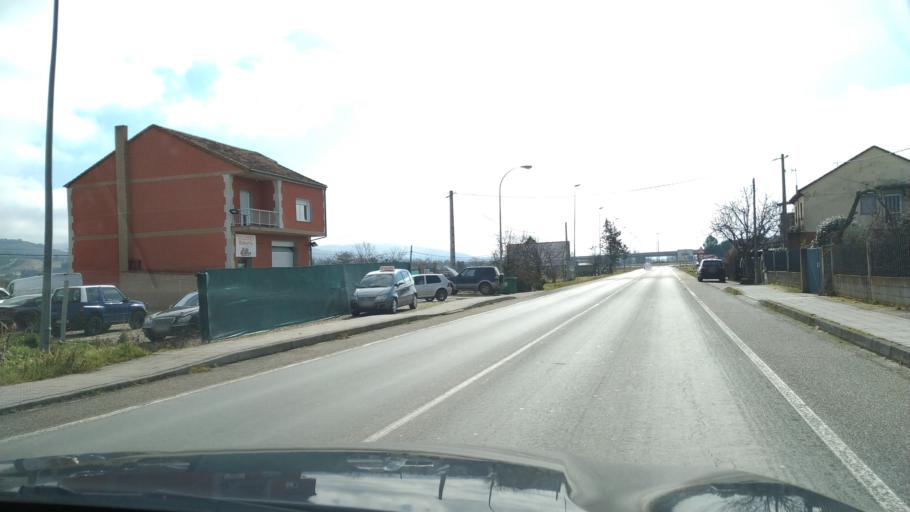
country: ES
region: Galicia
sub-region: Provincia de Ourense
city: Verin
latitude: 41.9168
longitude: -7.4434
